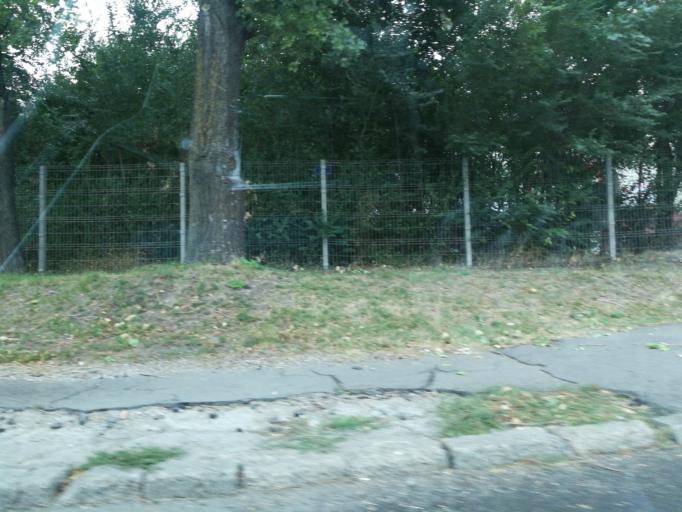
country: RO
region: Galati
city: Galati
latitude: 45.4471
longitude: 28.0115
